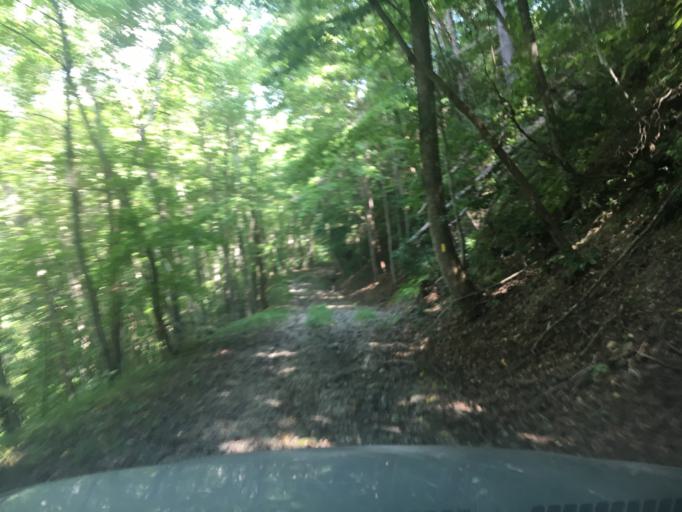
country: US
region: North Carolina
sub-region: Graham County
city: Robbinsville
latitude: 35.2682
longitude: -83.6832
